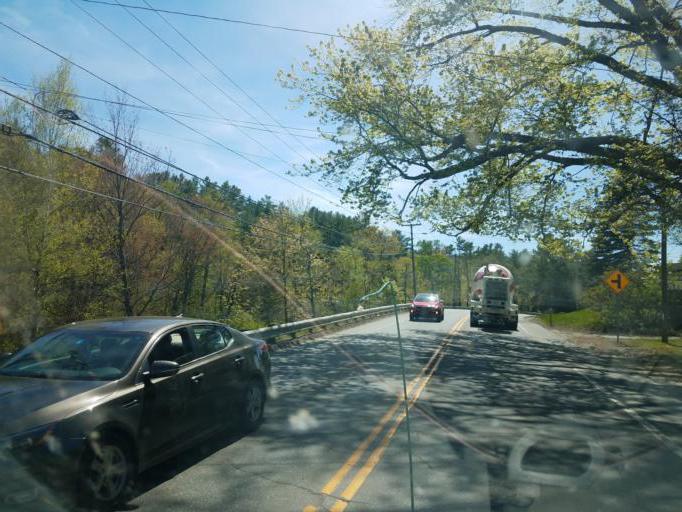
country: US
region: New Hampshire
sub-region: Grafton County
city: Grafton
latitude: 43.6467
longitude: -72.0215
